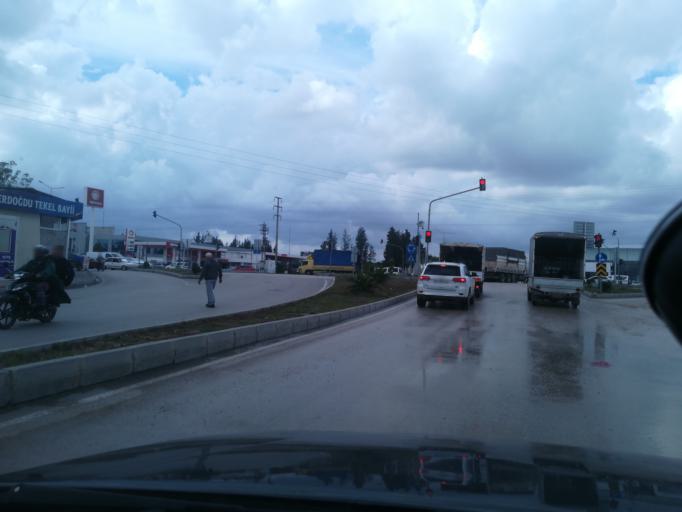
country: TR
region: Adana
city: Yuregir
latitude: 36.9827
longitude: 35.3942
